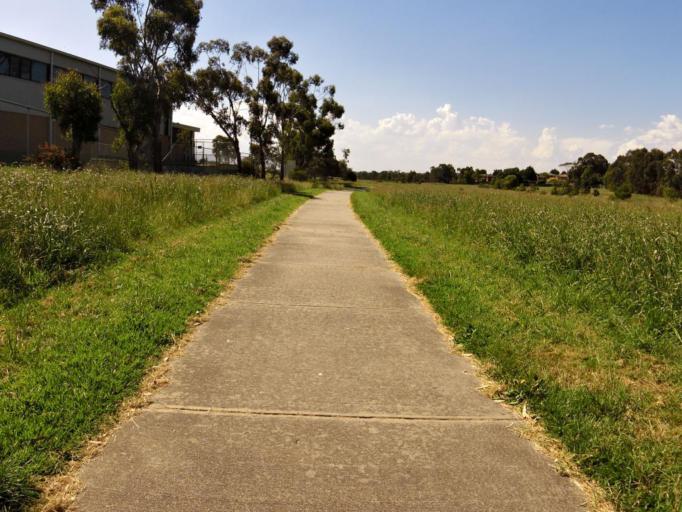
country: AU
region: Victoria
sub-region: Casey
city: Narre Warren South
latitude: -38.0437
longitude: 145.2760
